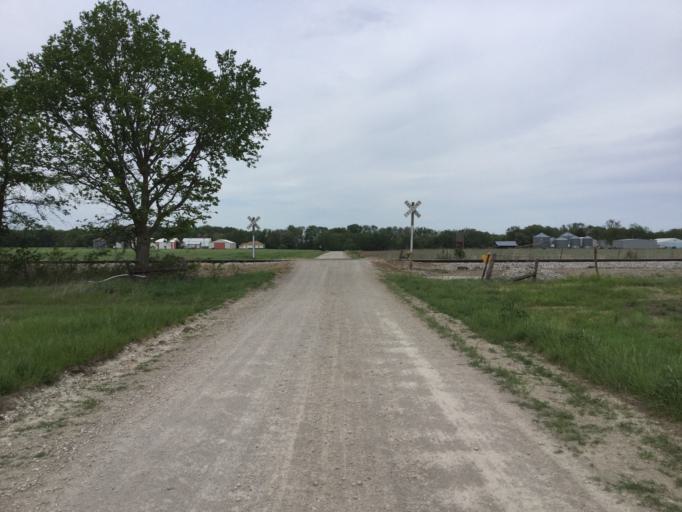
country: US
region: Kansas
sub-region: Montgomery County
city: Cherryvale
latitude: 37.2618
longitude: -95.5854
